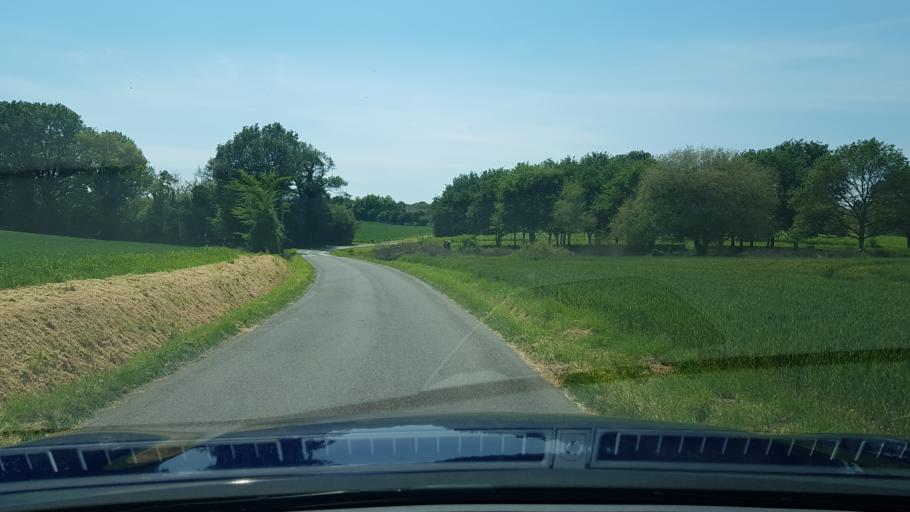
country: FR
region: Brittany
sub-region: Departement du Morbihan
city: Gestel
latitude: 47.8111
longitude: -3.4263
